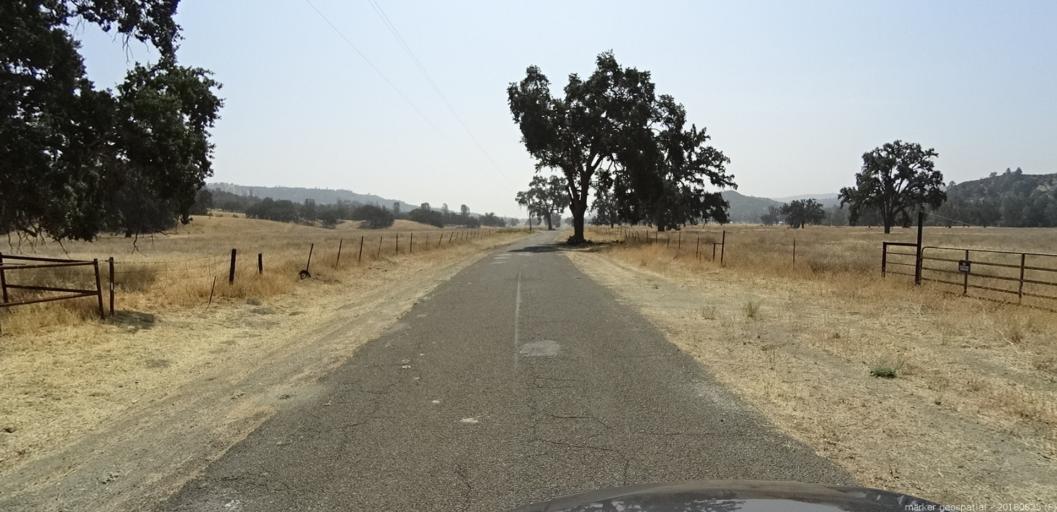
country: US
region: California
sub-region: Fresno County
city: Coalinga
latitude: 35.9352
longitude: -120.5136
